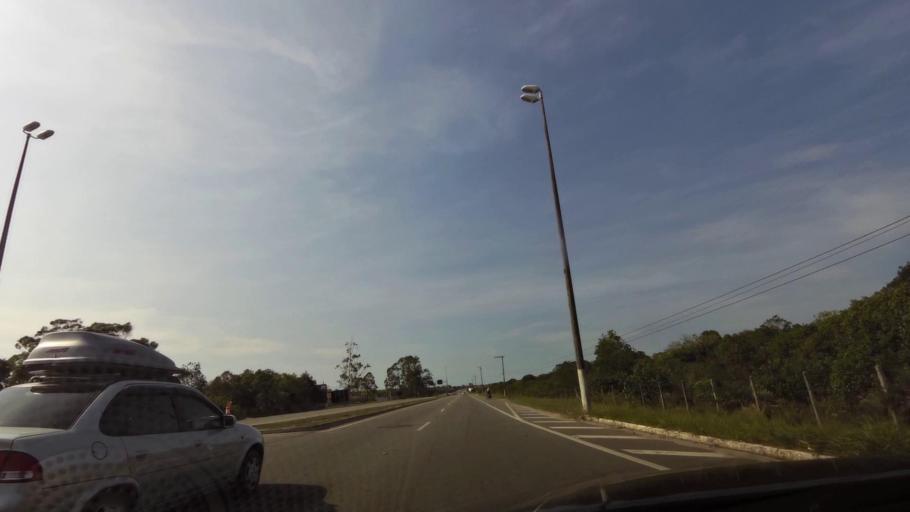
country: BR
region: Espirito Santo
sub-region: Guarapari
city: Guarapari
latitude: -20.5409
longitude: -40.3916
